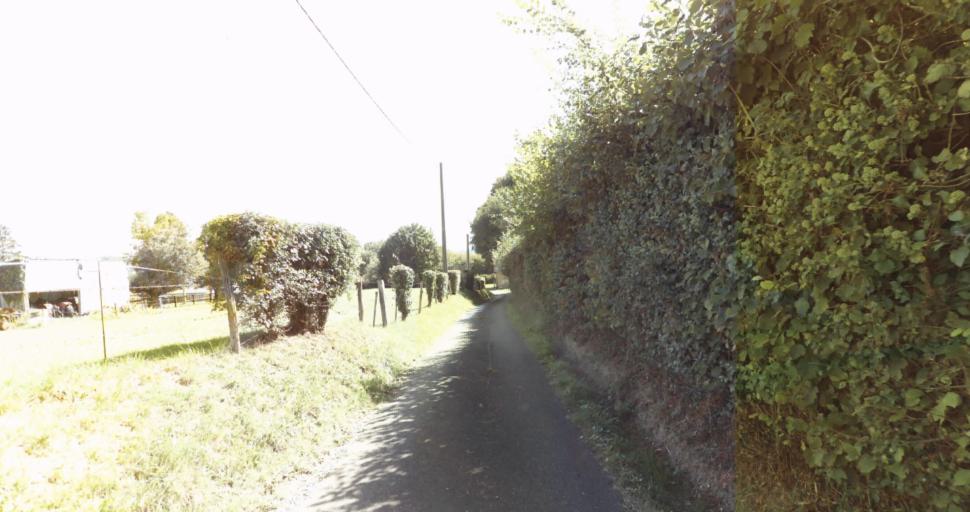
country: FR
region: Lower Normandy
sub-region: Departement de l'Orne
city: Gace
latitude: 48.7363
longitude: 0.2584
